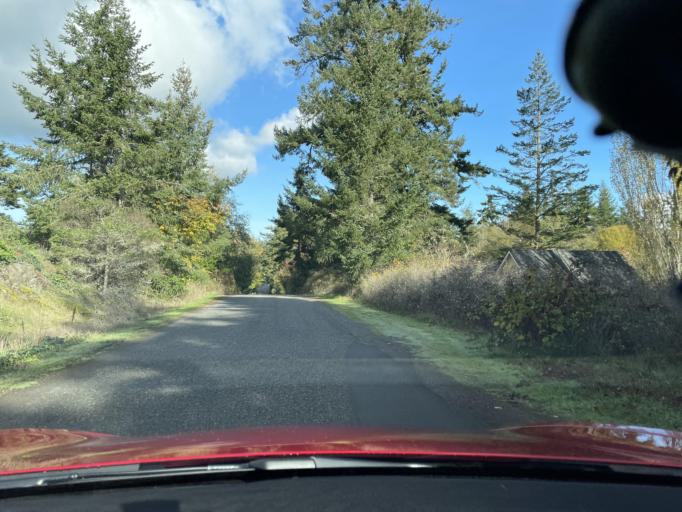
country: US
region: Washington
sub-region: San Juan County
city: Friday Harbor
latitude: 48.4995
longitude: -123.0230
